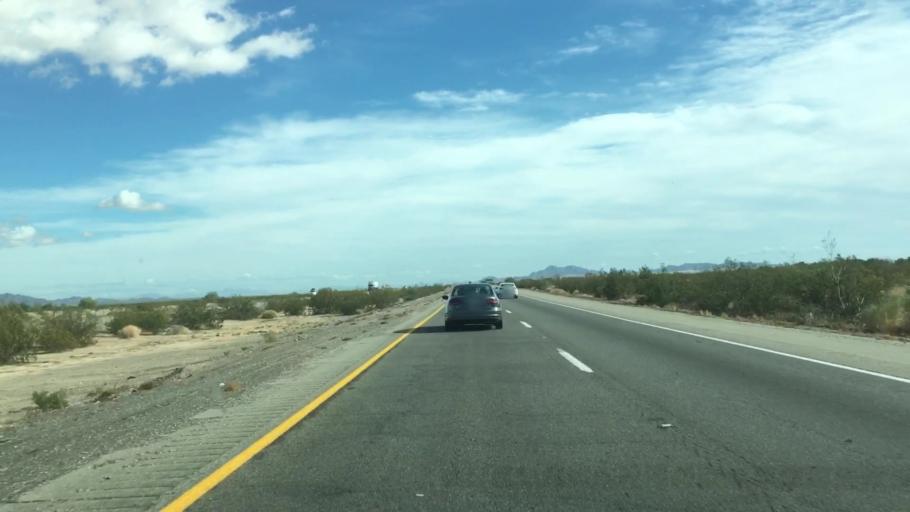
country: US
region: California
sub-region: Riverside County
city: Mesa Verde
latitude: 33.6185
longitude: -115.0281
